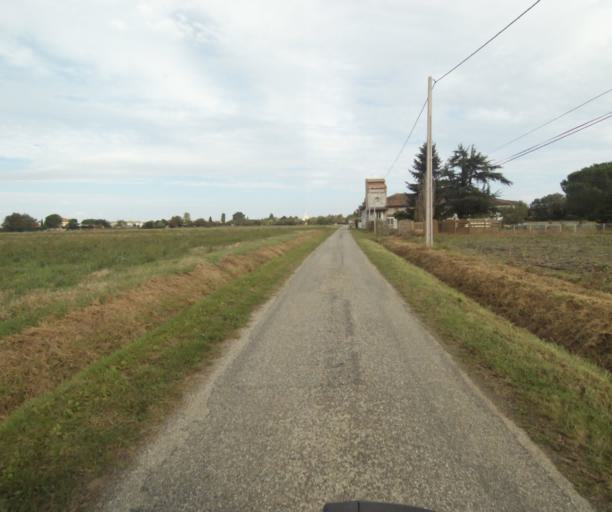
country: FR
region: Midi-Pyrenees
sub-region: Departement du Tarn-et-Garonne
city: Montech
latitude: 43.9407
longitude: 1.2218
